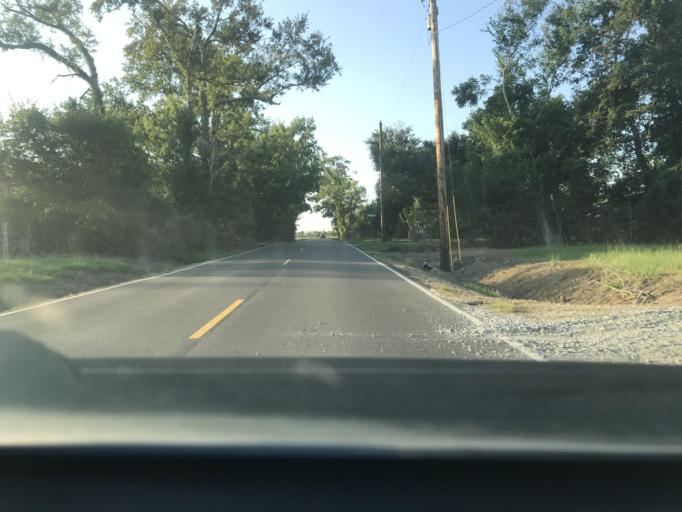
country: US
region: Louisiana
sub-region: Calcasieu Parish
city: Moss Bluff
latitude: 30.2621
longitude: -93.1954
